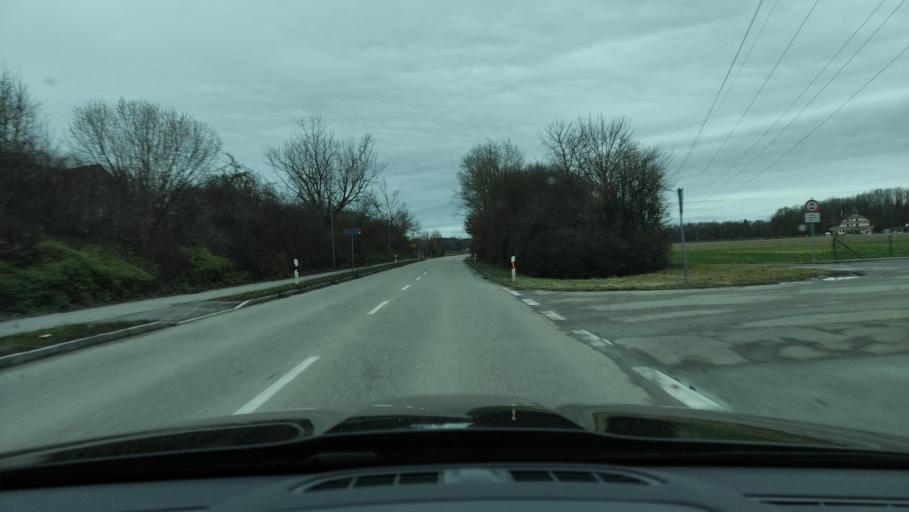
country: DE
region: Bavaria
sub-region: Swabia
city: Illertissen
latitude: 48.2123
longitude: 10.0914
